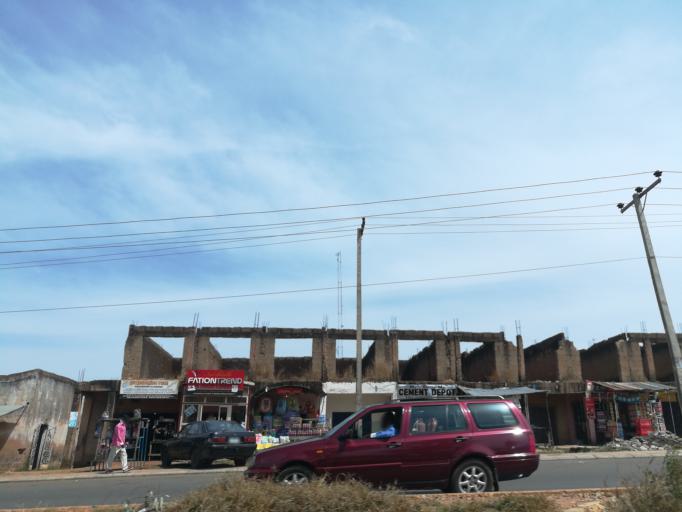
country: NG
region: Plateau
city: Bukuru
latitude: 9.8143
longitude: 8.8661
